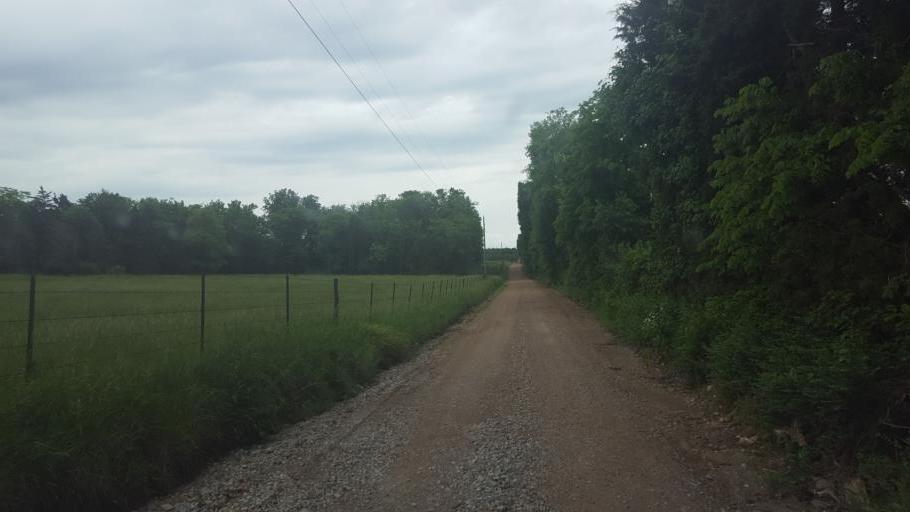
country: US
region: Missouri
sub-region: Moniteau County
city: California
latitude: 38.6837
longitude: -92.5982
